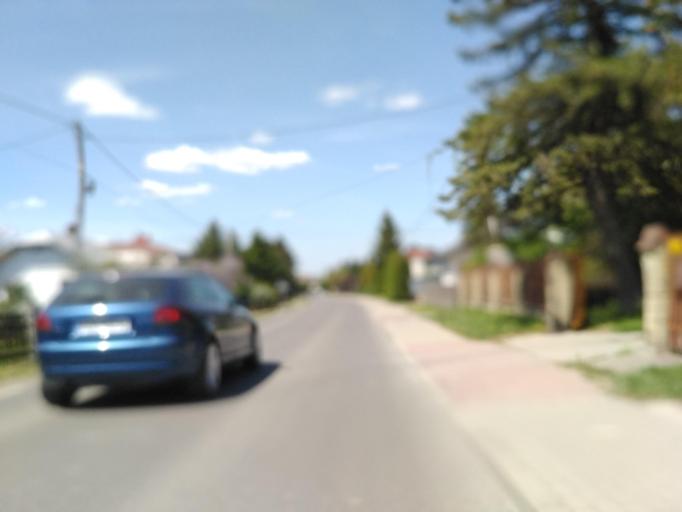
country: PL
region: Subcarpathian Voivodeship
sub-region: Powiat krosnienski
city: Jedlicze
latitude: 49.6941
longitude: 21.6828
